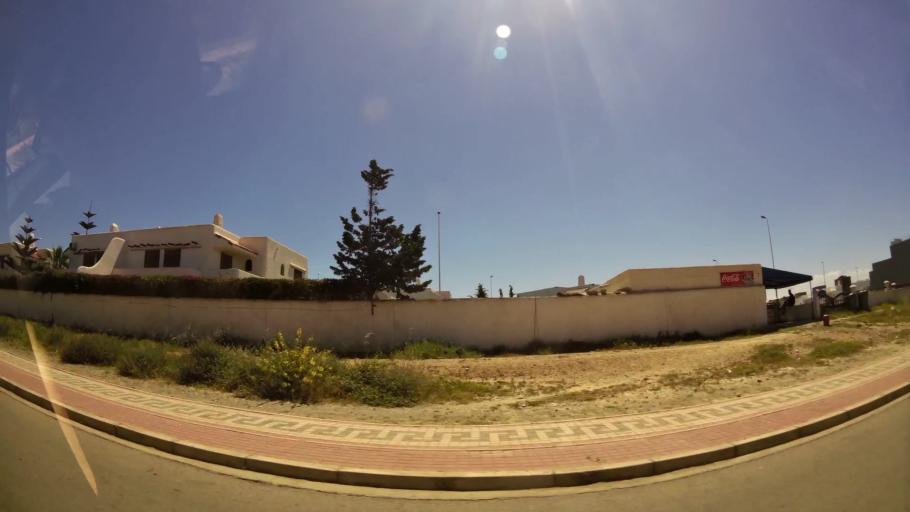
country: MA
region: Oriental
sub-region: Berkane-Taourirt
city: Madagh
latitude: 35.0955
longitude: -2.2651
